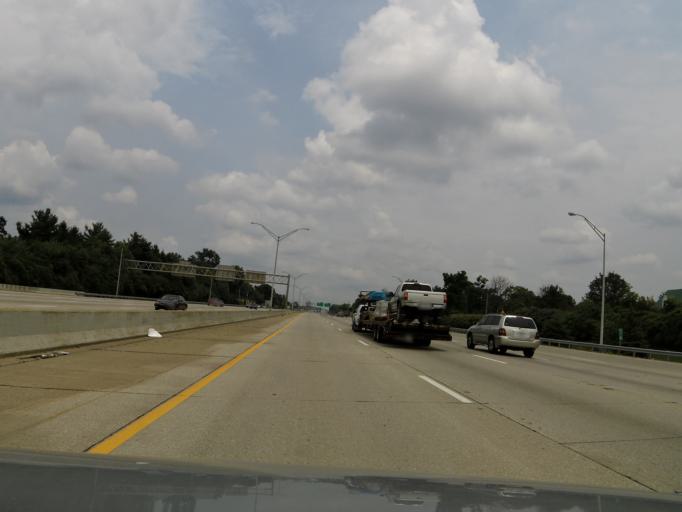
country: US
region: Kentucky
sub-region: Jefferson County
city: West Buechel
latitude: 38.2127
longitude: -85.6681
